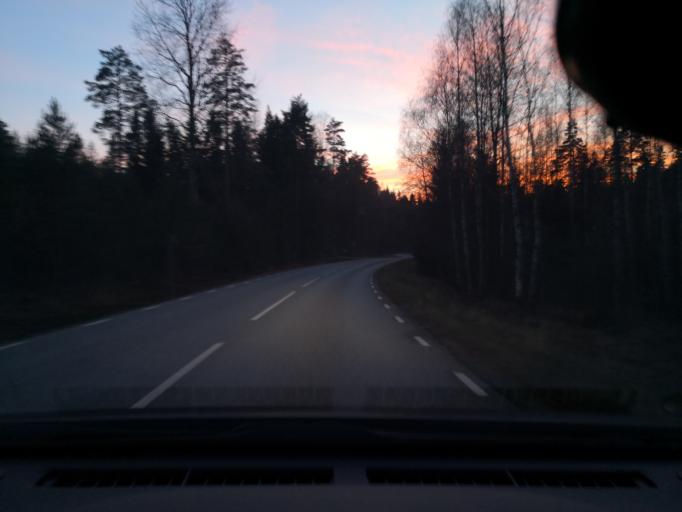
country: SE
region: OErebro
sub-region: Lindesbergs Kommun
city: Fellingsbro
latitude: 59.4067
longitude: 15.5383
